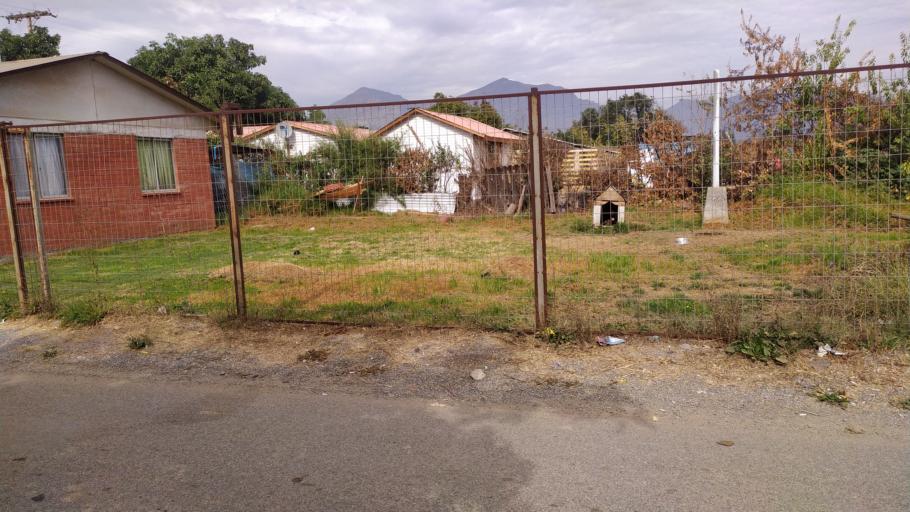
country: CL
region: Valparaiso
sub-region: Provincia de San Felipe
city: Llaillay
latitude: -32.7831
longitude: -70.9132
